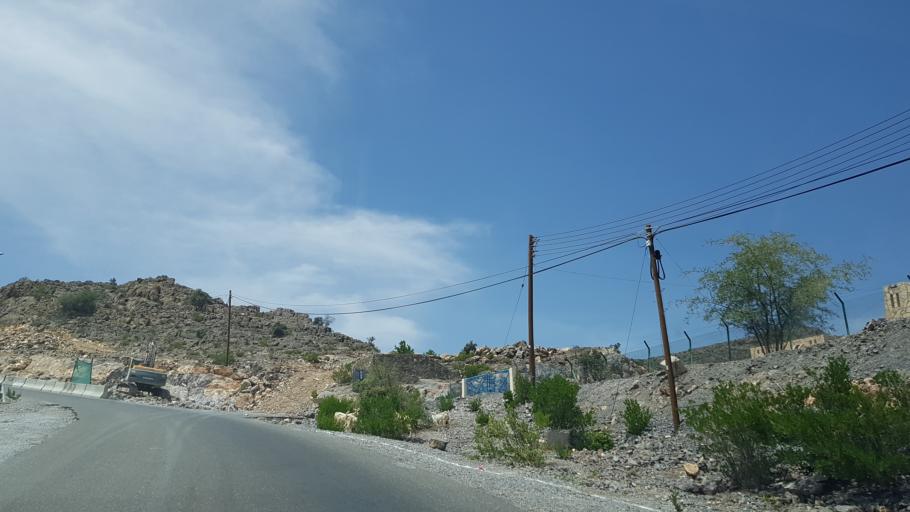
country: OM
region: Muhafazat ad Dakhiliyah
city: Izki
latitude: 23.0945
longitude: 57.6826
